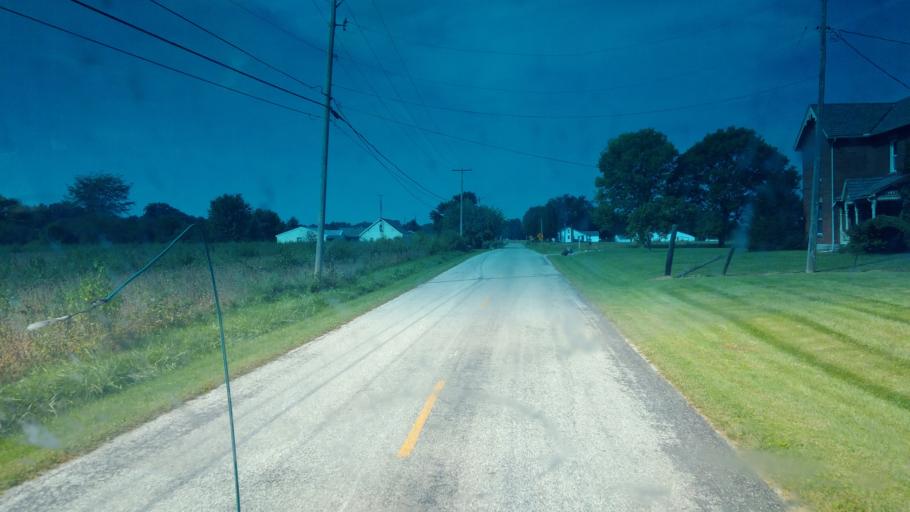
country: US
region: Ohio
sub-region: Morrow County
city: Cardington
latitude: 40.6384
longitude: -82.9729
